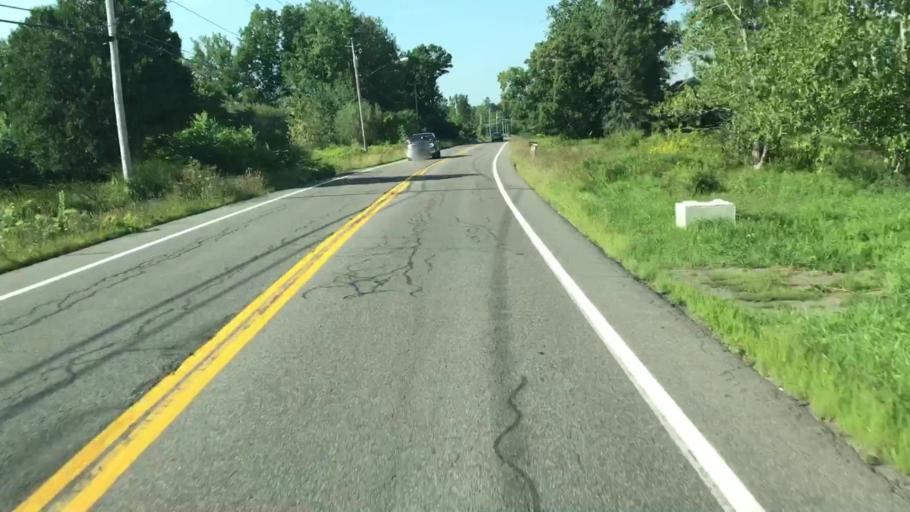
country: US
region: New York
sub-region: Onondaga County
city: Skaneateles
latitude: 42.9692
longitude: -76.4295
